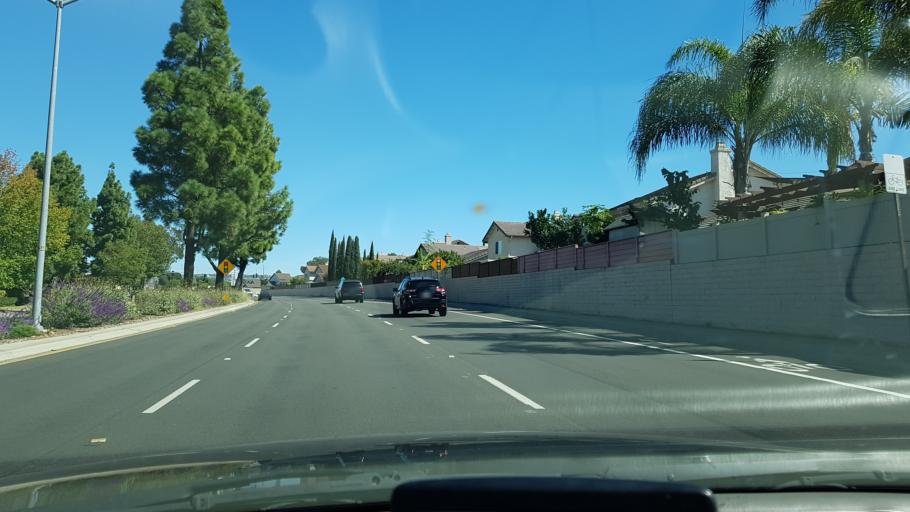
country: US
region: California
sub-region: San Diego County
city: Fairbanks Ranch
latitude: 32.9098
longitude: -117.1577
